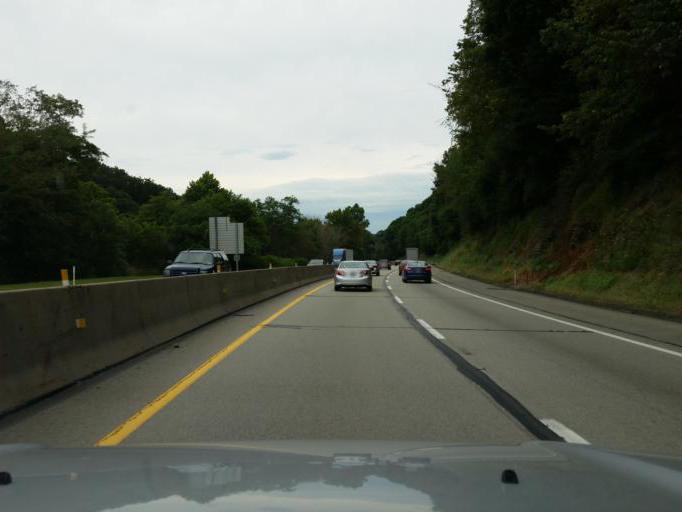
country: US
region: Pennsylvania
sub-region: Westmoreland County
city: Level Green
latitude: 40.4262
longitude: -79.7385
